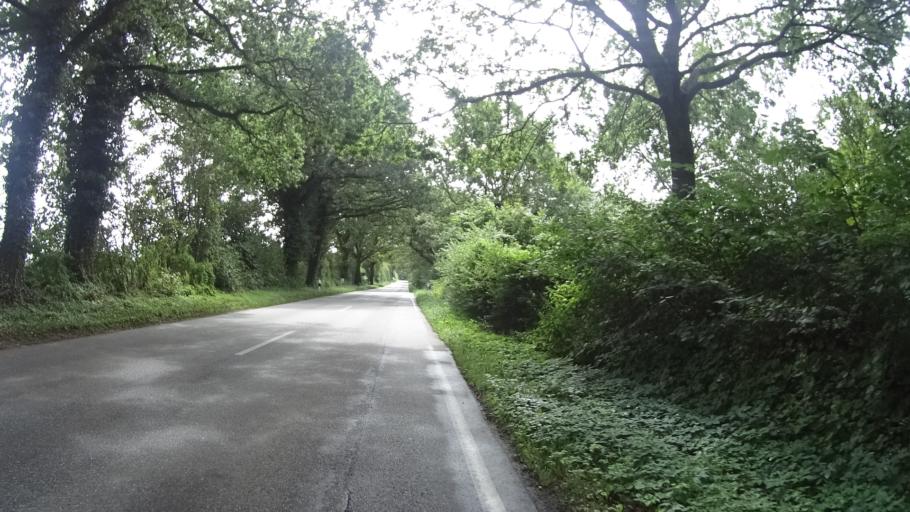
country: DE
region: Schleswig-Holstein
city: Tangstedt
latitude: 53.7419
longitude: 10.0700
